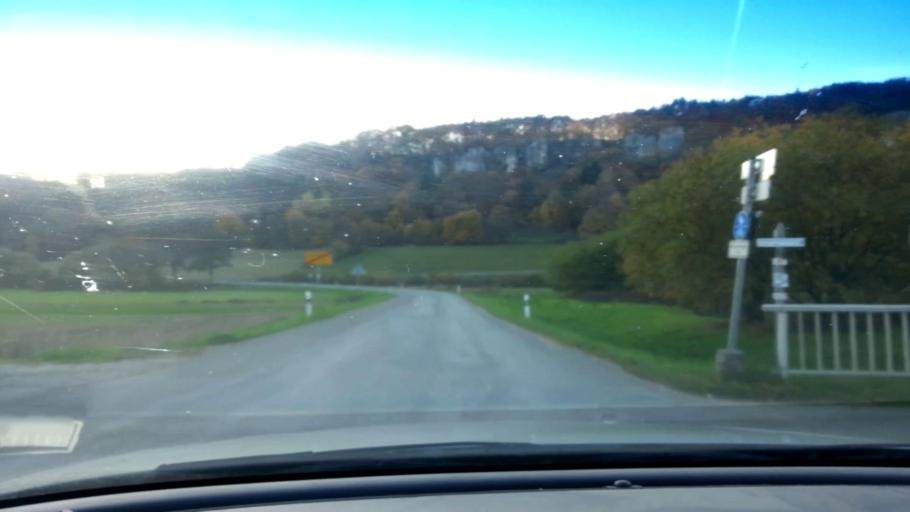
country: DE
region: Bavaria
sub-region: Upper Franconia
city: Unterleinleiter
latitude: 49.8404
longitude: 11.1968
